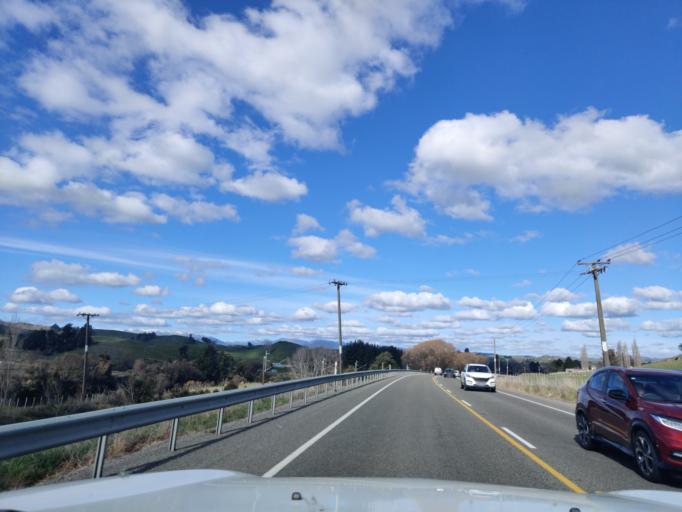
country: NZ
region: Manawatu-Wanganui
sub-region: Ruapehu District
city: Waiouru
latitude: -39.7114
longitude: 175.8372
